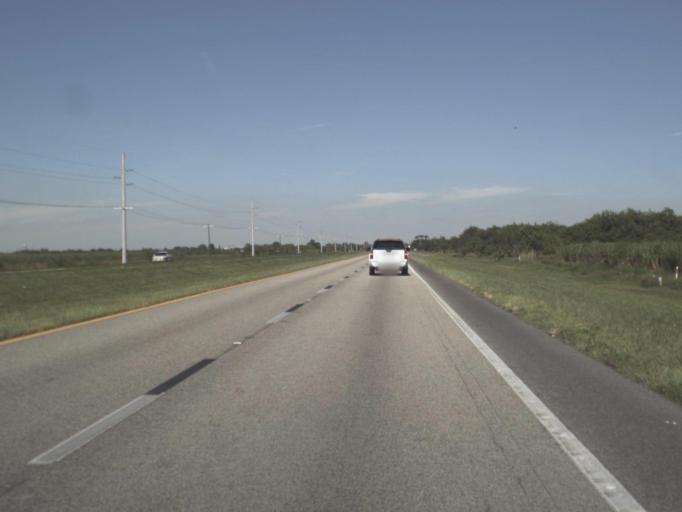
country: US
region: Florida
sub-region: Glades County
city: Moore Haven
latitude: 26.7964
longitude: -81.0826
